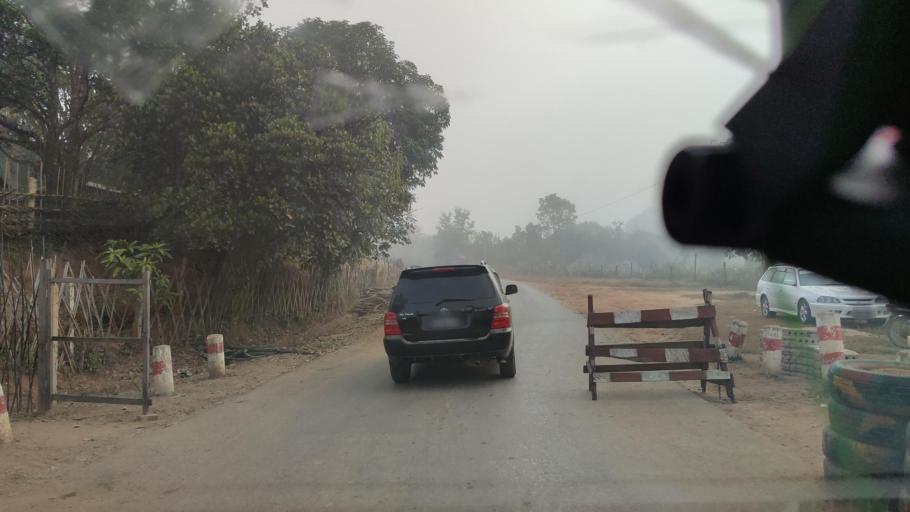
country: MM
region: Shan
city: Taunggyi
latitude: 21.2788
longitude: 97.7002
